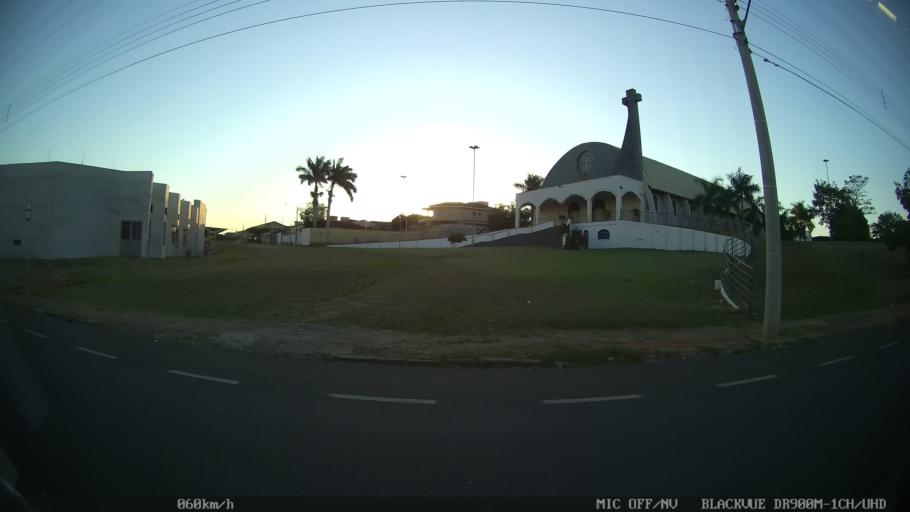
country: BR
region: Sao Paulo
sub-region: Sao Jose Do Rio Preto
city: Sao Jose do Rio Preto
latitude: -20.8049
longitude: -49.3606
